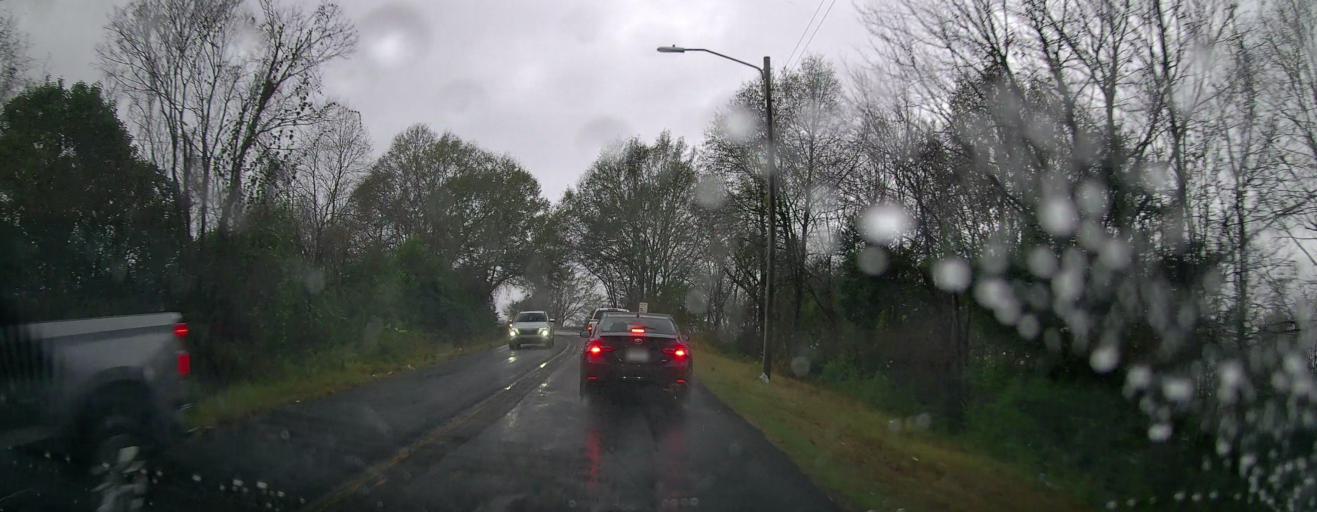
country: US
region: Alabama
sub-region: Montgomery County
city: Montgomery
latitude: 32.3699
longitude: -86.3514
